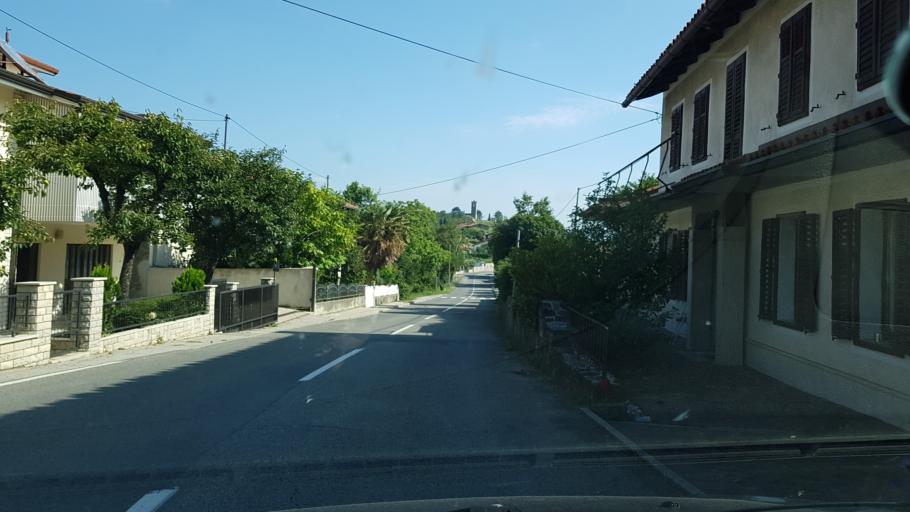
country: IT
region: Friuli Venezia Giulia
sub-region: Provincia di Gorizia
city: San Floriano del Collio
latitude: 46.0103
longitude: 13.5741
